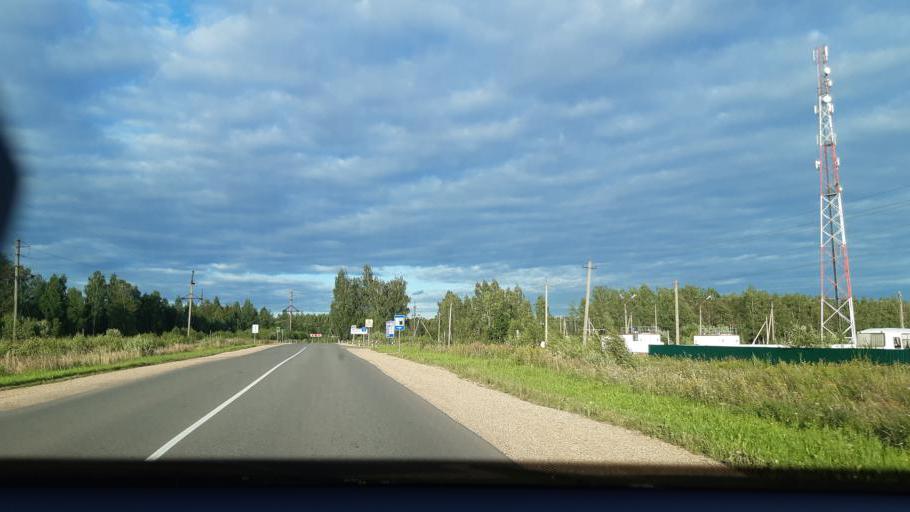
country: RU
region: Smolensk
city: Yel'nya
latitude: 54.5945
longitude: 33.1863
